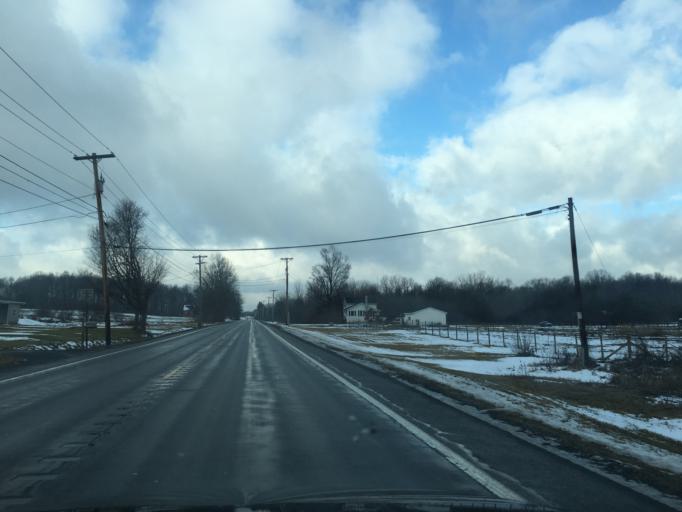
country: US
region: New York
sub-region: Ontario County
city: Manchester
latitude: 42.9671
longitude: -77.2793
